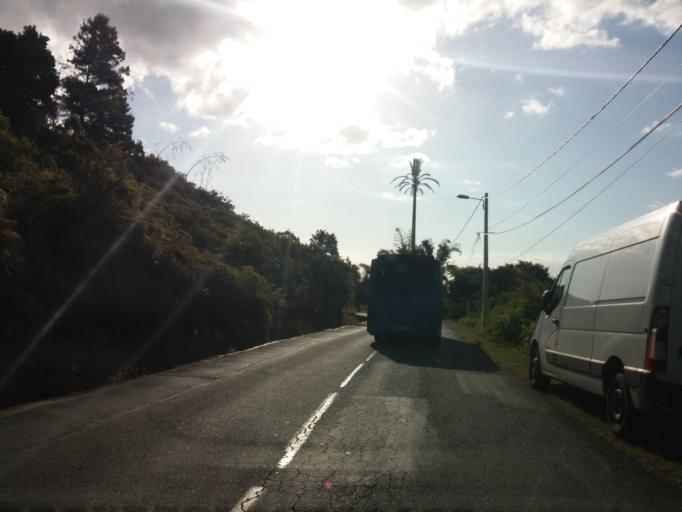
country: RE
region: Reunion
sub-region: Reunion
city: Saint-Denis
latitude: -20.8873
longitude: 55.4190
